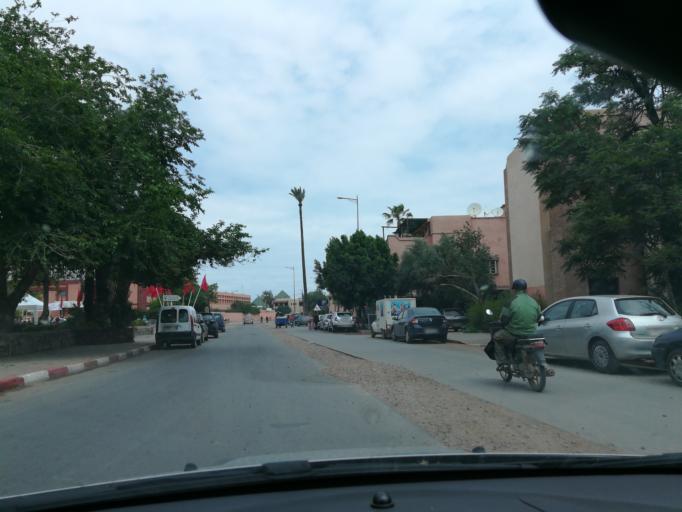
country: MA
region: Marrakech-Tensift-Al Haouz
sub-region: Marrakech
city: Marrakesh
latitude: 31.6298
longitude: -7.9976
